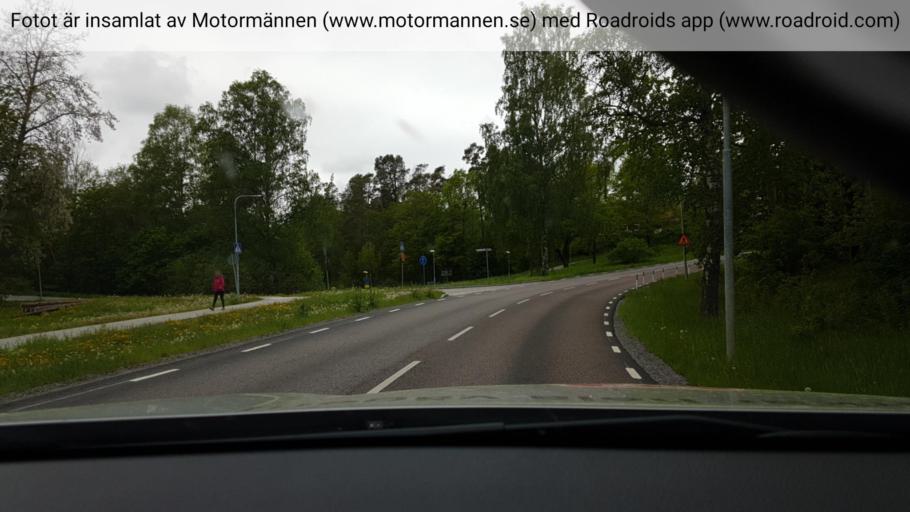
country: SE
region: Stockholm
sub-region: Lidingo
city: Brevik
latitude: 59.3490
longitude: 18.1704
